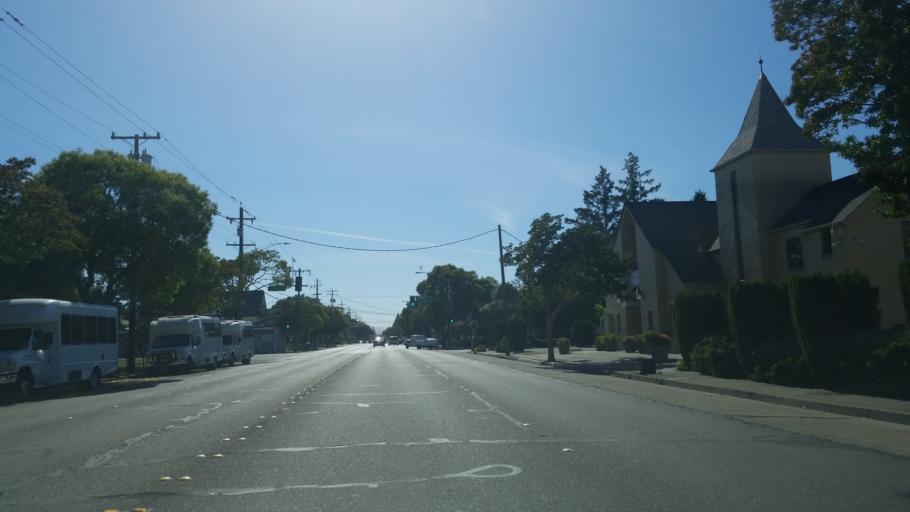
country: US
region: California
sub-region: Sonoma County
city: Santa Rosa
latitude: 38.4455
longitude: -122.7100
